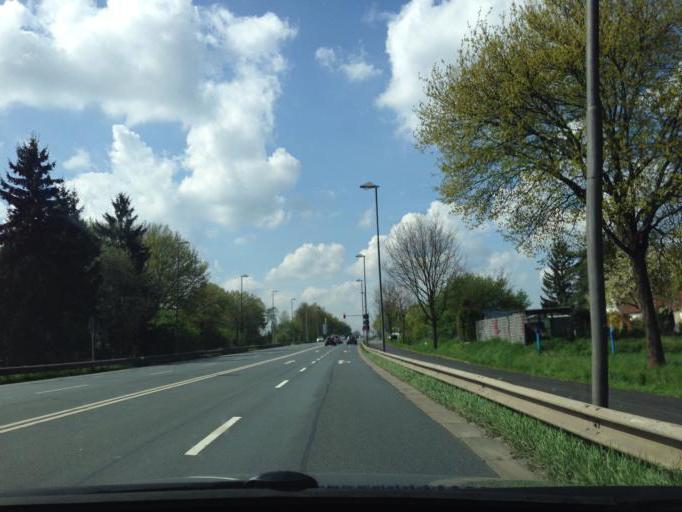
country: DE
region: Lower Saxony
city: Celle
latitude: 52.6065
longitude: 10.0659
